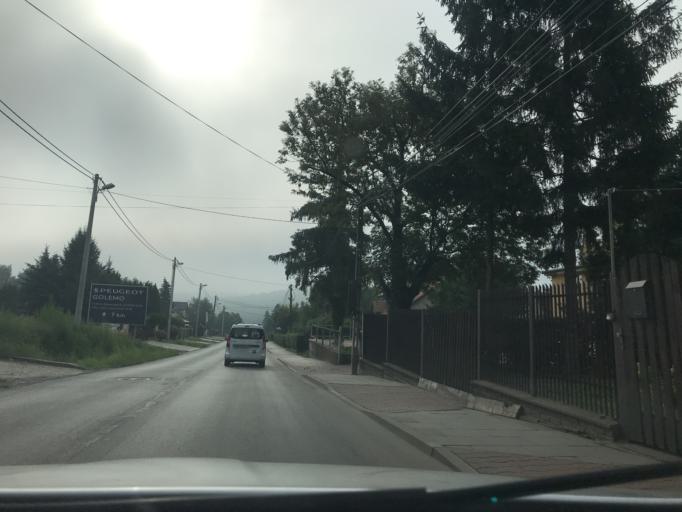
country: PL
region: Lesser Poland Voivodeship
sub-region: Powiat krakowski
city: Ochojno
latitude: 50.0033
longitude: 19.9955
